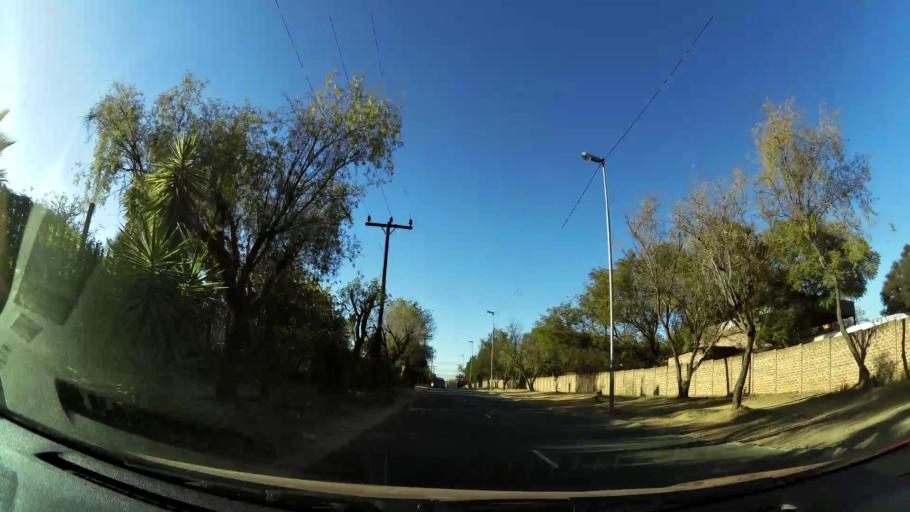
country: ZA
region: Gauteng
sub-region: City of Johannesburg Metropolitan Municipality
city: Midrand
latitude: -26.0243
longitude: 28.1477
